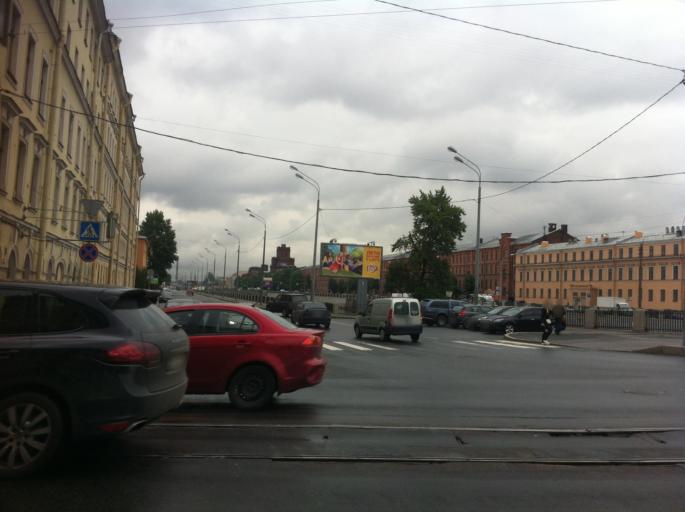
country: RU
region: St.-Petersburg
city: Admiralteisky
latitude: 59.9096
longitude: 30.2756
